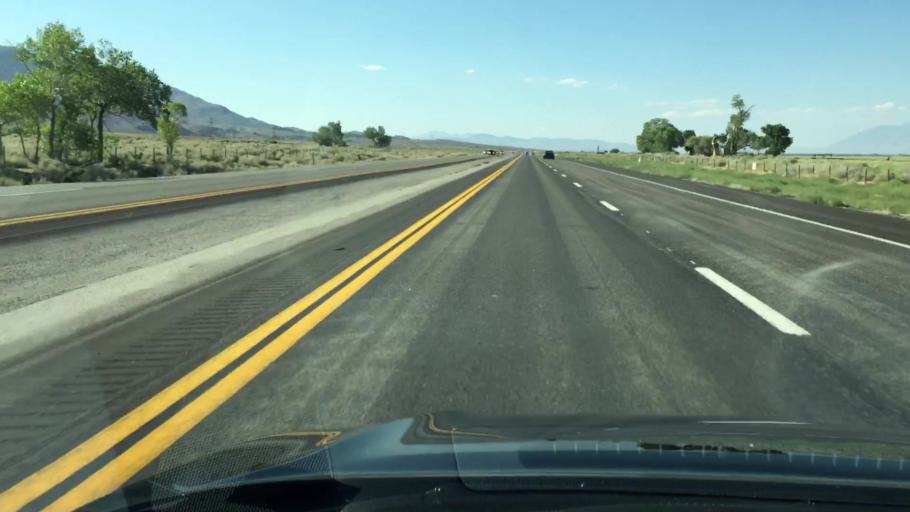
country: US
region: California
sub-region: Inyo County
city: Big Pine
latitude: 37.2418
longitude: -118.3511
